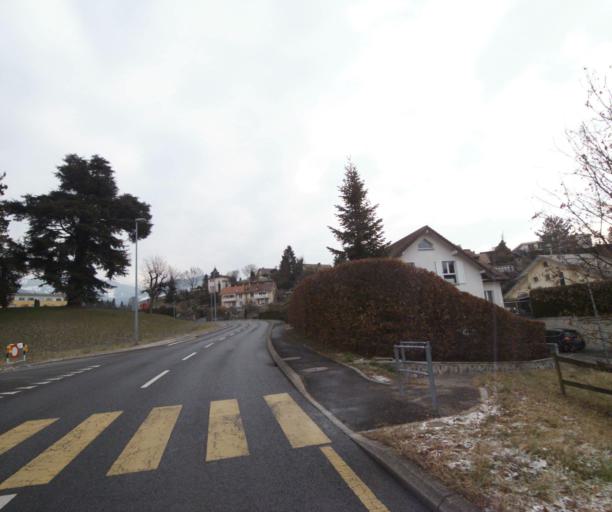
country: CH
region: Vaud
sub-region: Riviera-Pays-d'Enhaut District
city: La Tour-de-Peilz
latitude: 46.4614
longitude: 6.8657
